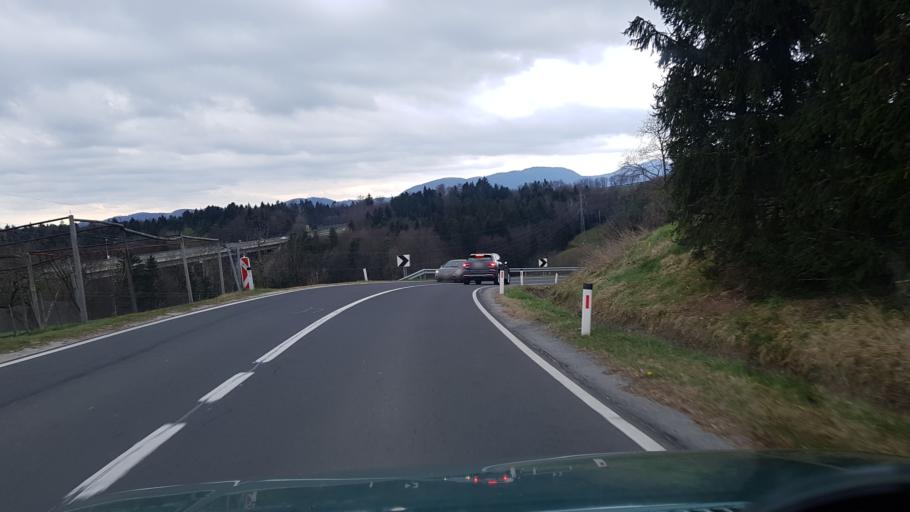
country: SI
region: Slovenska Bistrica
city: Slovenska Bistrica
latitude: 46.3682
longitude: 15.5198
